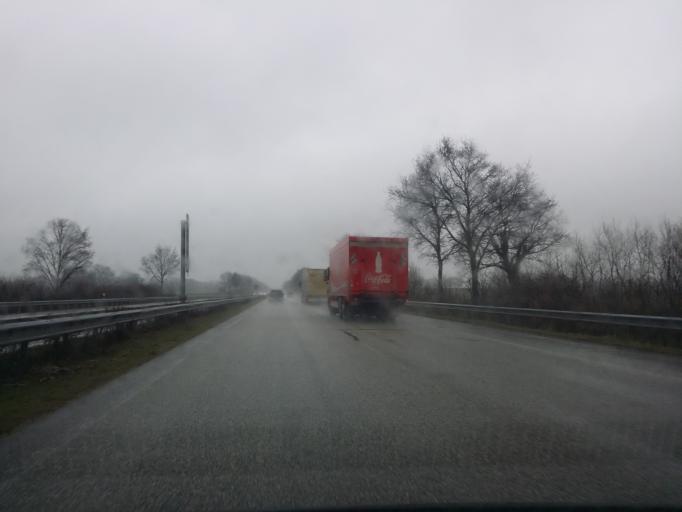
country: DE
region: Schleswig-Holstein
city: Manhagen
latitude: 54.2050
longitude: 10.8995
